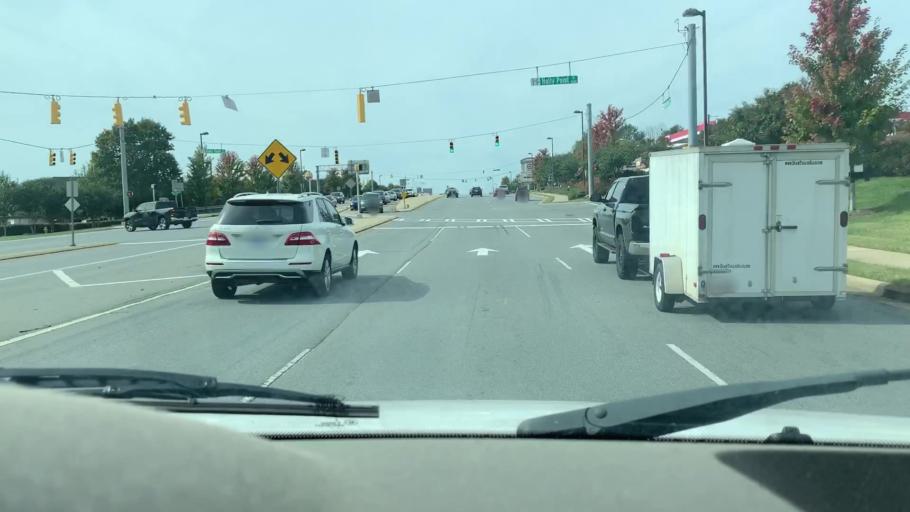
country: US
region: North Carolina
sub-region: Mecklenburg County
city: Huntersville
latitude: 35.4422
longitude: -80.8627
